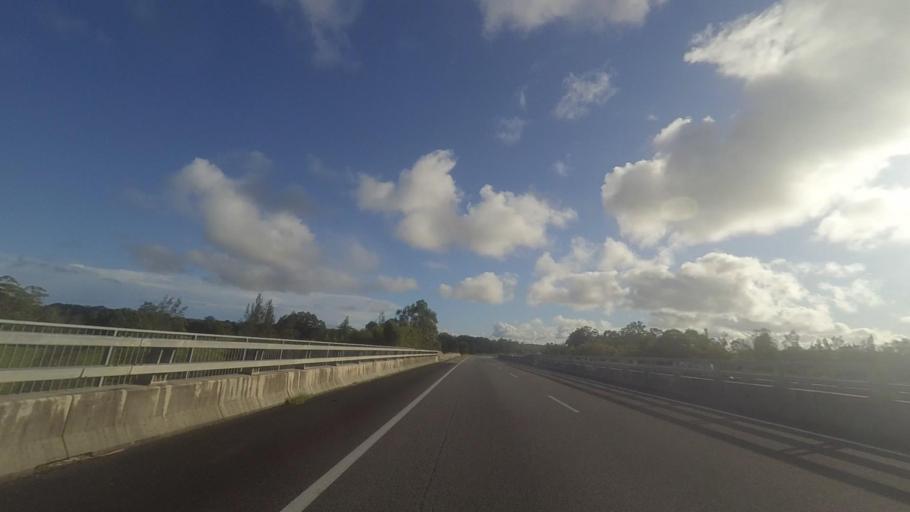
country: AU
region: New South Wales
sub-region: Great Lakes
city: Nabiac
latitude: -32.1058
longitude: 152.3741
